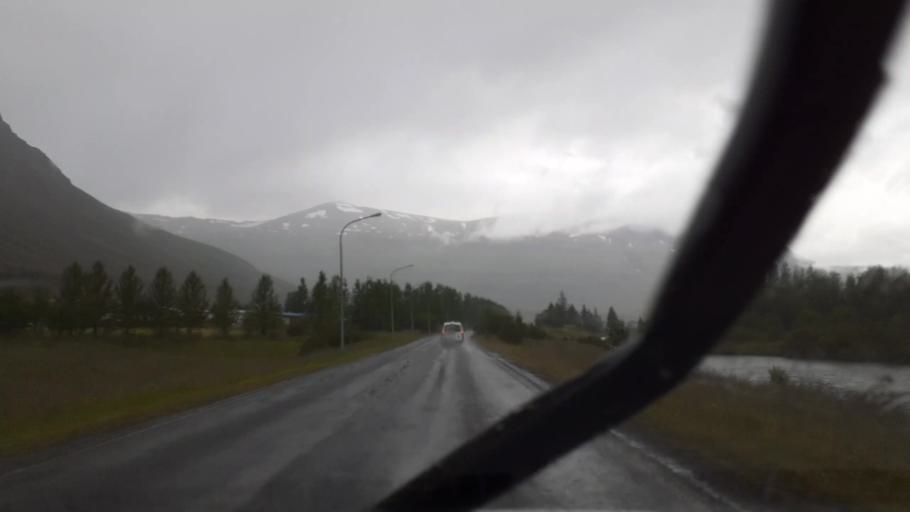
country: IS
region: East
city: Eskifjoerdur
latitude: 65.2556
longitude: -14.0134
